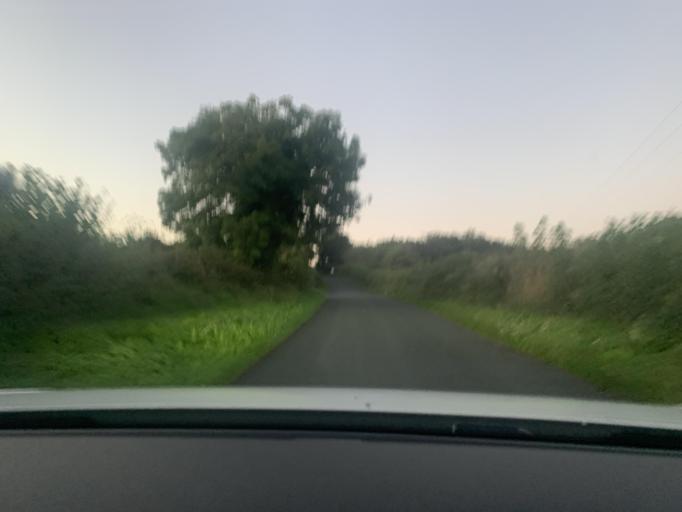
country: IE
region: Connaught
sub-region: County Leitrim
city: Manorhamilton
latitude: 54.2712
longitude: -8.2839
